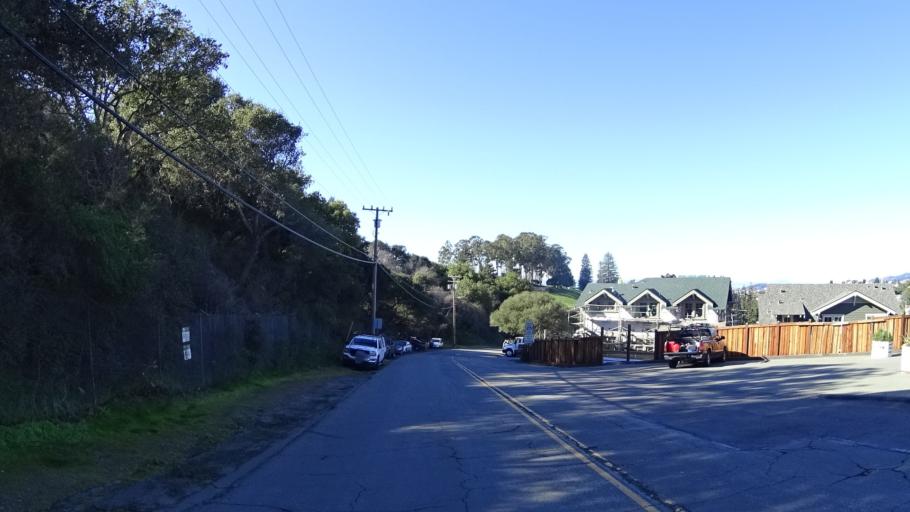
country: US
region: California
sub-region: Alameda County
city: Piedmont
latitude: 37.8362
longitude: -122.2307
